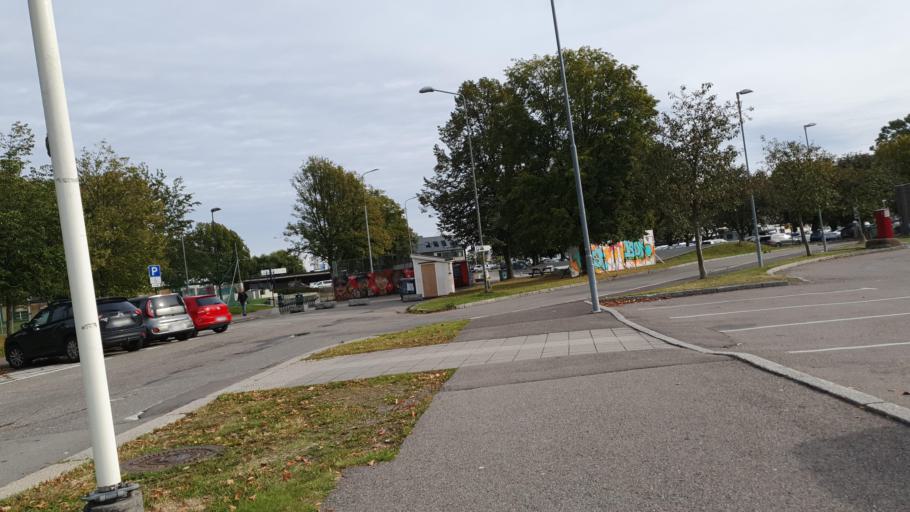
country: NO
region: Vestfold
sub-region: Tonsberg
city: Tonsberg
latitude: 59.2639
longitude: 10.4150
